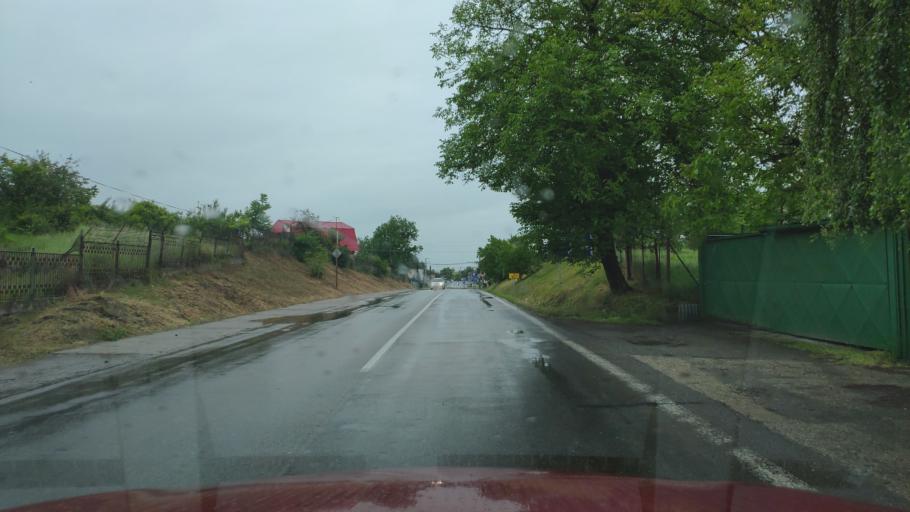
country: HU
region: Borsod-Abauj-Zemplen
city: Ricse
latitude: 48.4310
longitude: 21.9757
